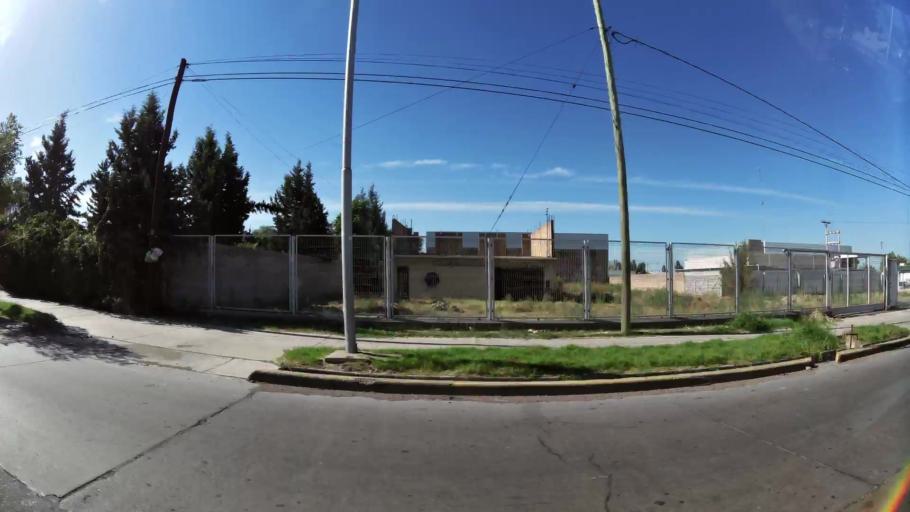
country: AR
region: Mendoza
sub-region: Departamento de Godoy Cruz
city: Godoy Cruz
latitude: -32.9312
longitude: -68.8018
